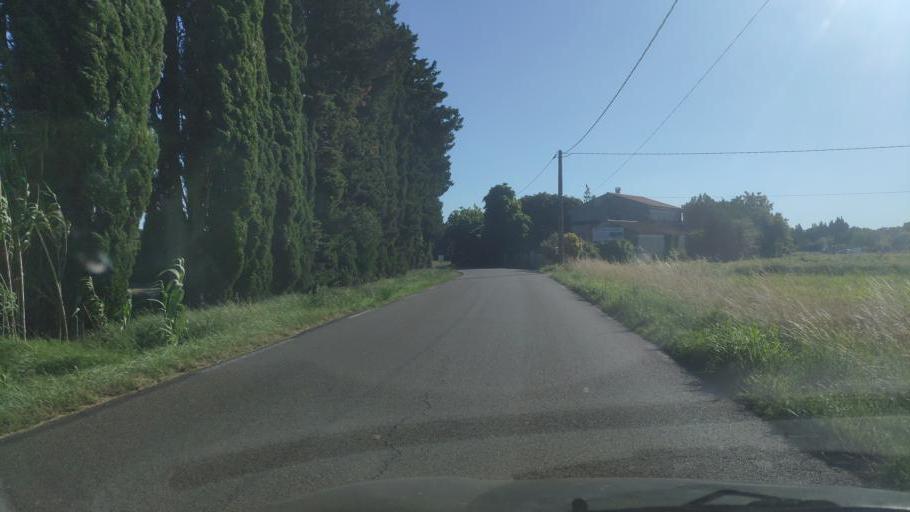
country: FR
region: Provence-Alpes-Cote d'Azur
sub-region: Departement du Vaucluse
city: Aubignan
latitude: 44.0850
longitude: 5.0144
